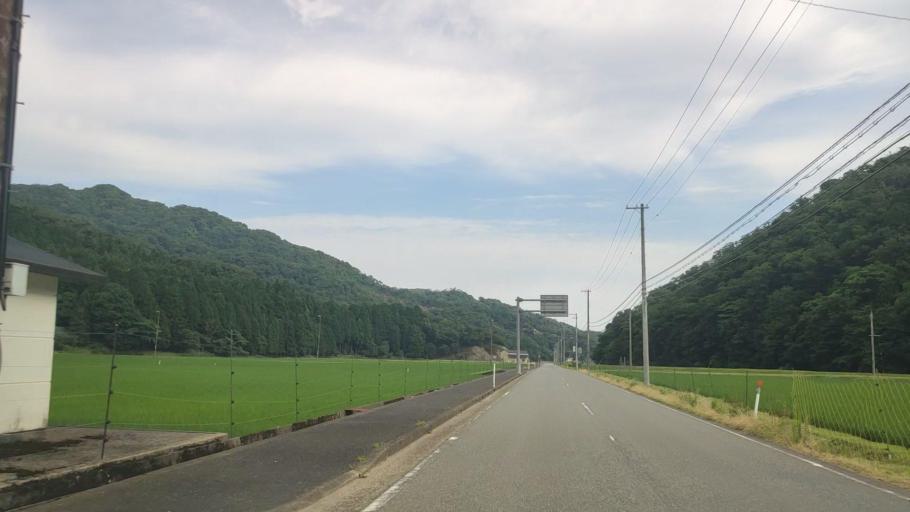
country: JP
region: Hyogo
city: Toyooka
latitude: 35.6164
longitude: 134.8435
